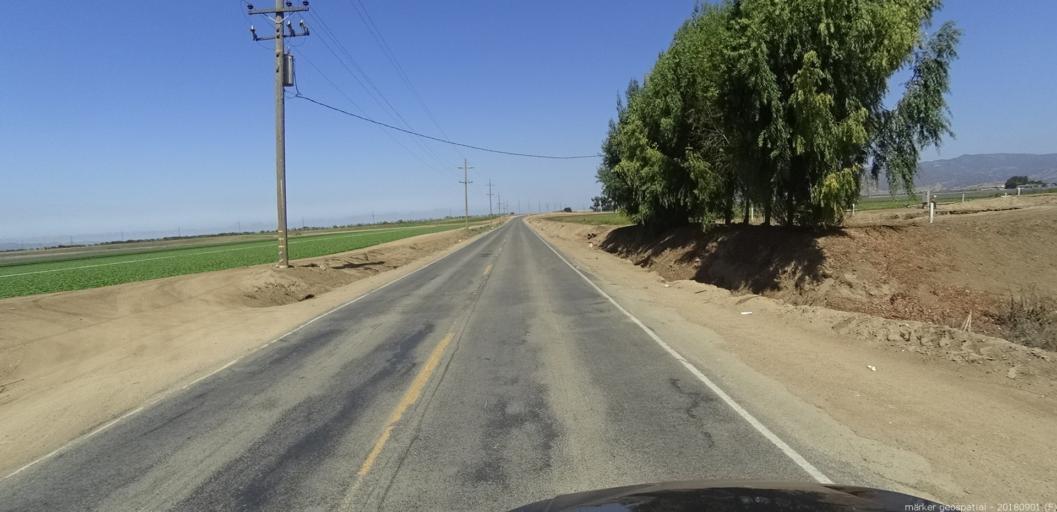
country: US
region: California
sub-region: Monterey County
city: Chualar
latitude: 36.5776
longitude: -121.4951
